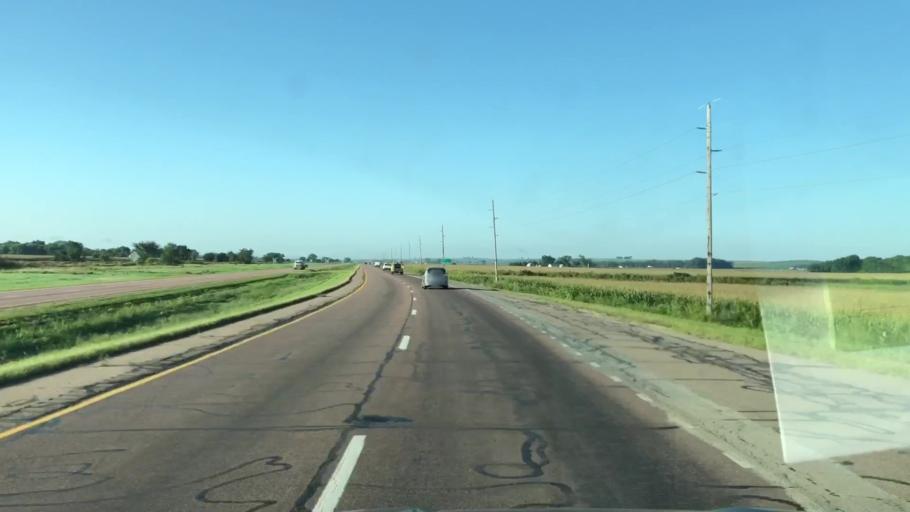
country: US
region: Iowa
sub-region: Plymouth County
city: Le Mars
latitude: 42.7123
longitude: -96.2516
